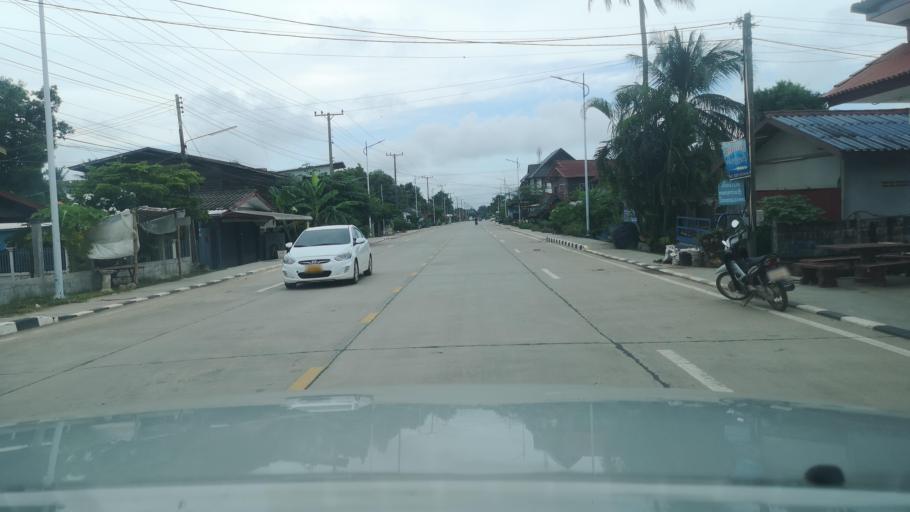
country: TH
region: Nong Khai
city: Tha Bo
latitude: 17.8301
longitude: 102.6480
